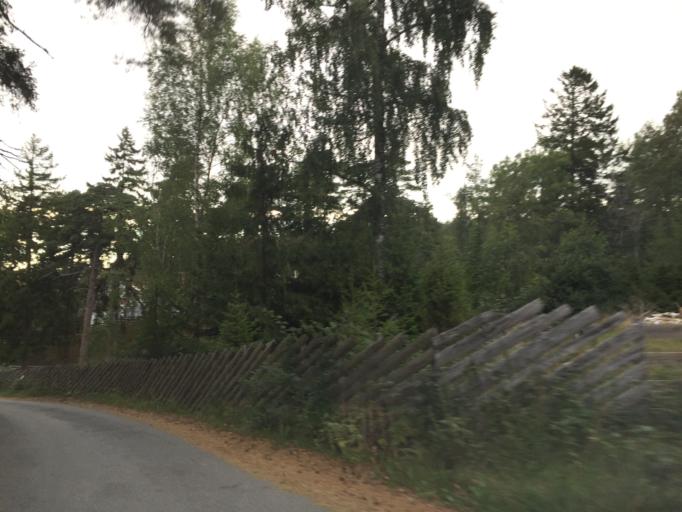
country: NO
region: Ostfold
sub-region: Hvaler
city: Skjaerhalden
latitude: 59.0589
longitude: 11.0075
